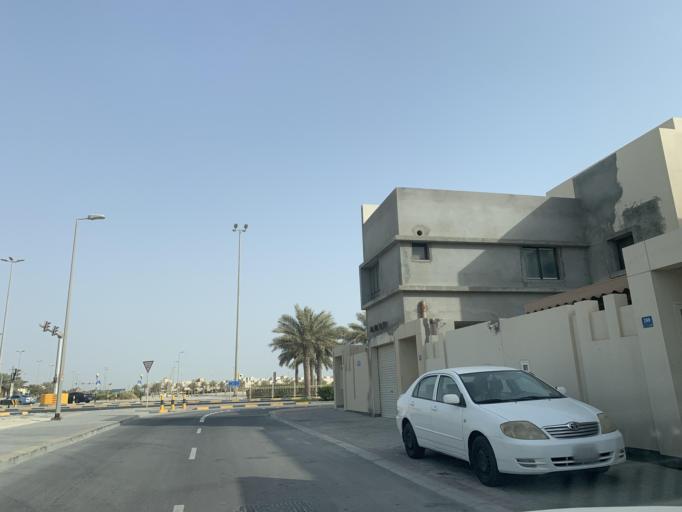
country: BH
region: Manama
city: Jidd Hafs
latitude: 26.2301
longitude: 50.4477
